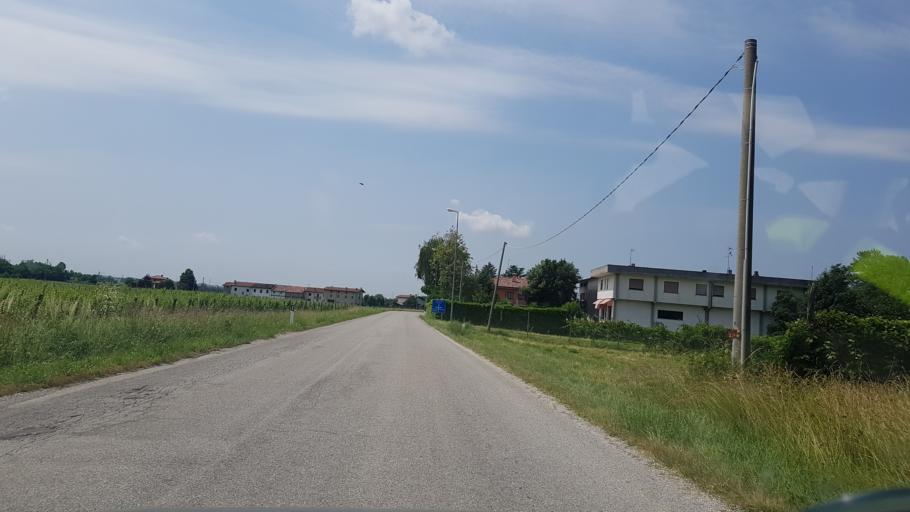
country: IT
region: Friuli Venezia Giulia
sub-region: Provincia di Udine
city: Torreano
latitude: 46.1138
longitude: 13.4119
